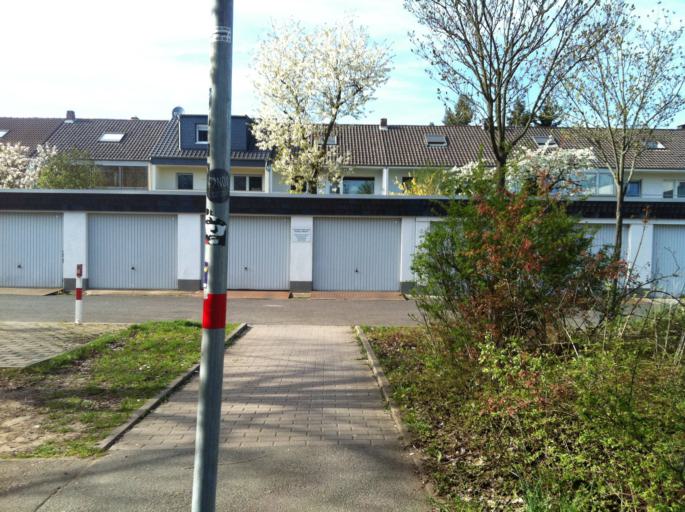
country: DE
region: Rheinland-Pfalz
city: Mainz
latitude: 49.9951
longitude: 8.2364
